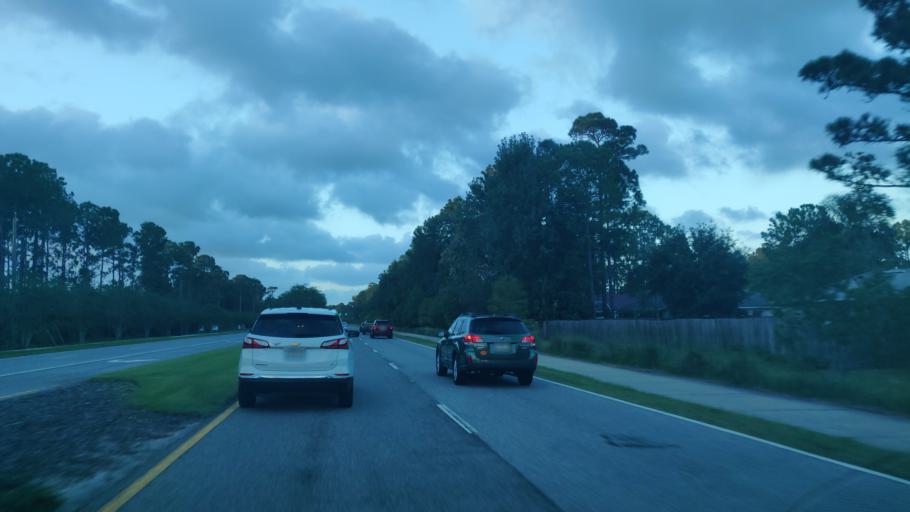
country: US
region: Florida
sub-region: Flagler County
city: Bunnell
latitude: 29.5014
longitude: -81.2198
